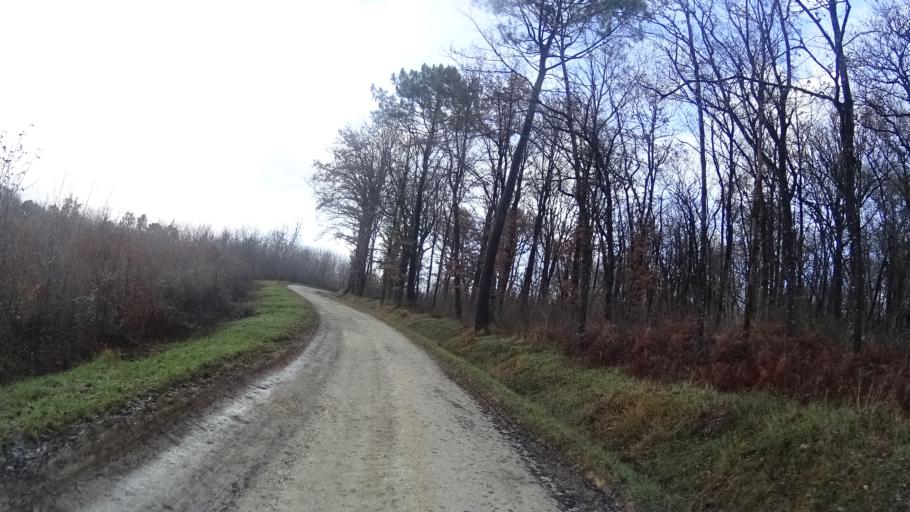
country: FR
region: Aquitaine
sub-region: Departement de la Dordogne
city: Antonne-et-Trigonant
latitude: 45.2127
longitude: 0.8704
